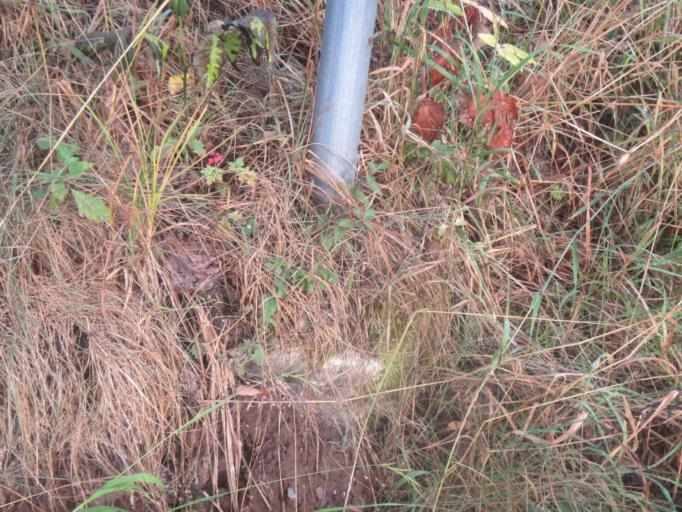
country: DE
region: Rheinland-Pfalz
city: Darstein
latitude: 49.1418
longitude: 7.8980
